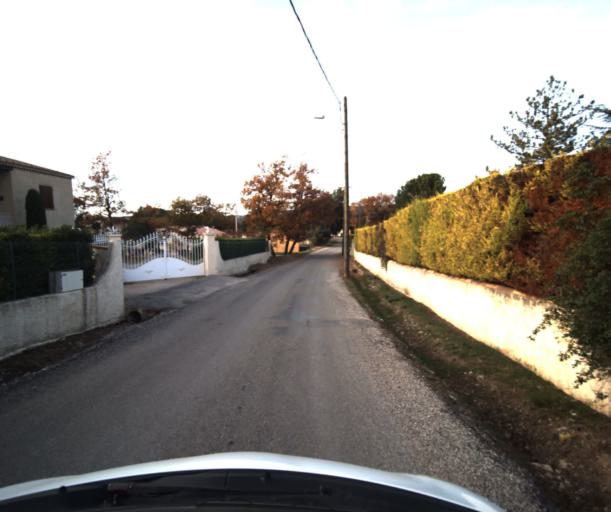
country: FR
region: Provence-Alpes-Cote d'Azur
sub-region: Departement du Vaucluse
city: Pertuis
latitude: 43.6943
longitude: 5.5349
